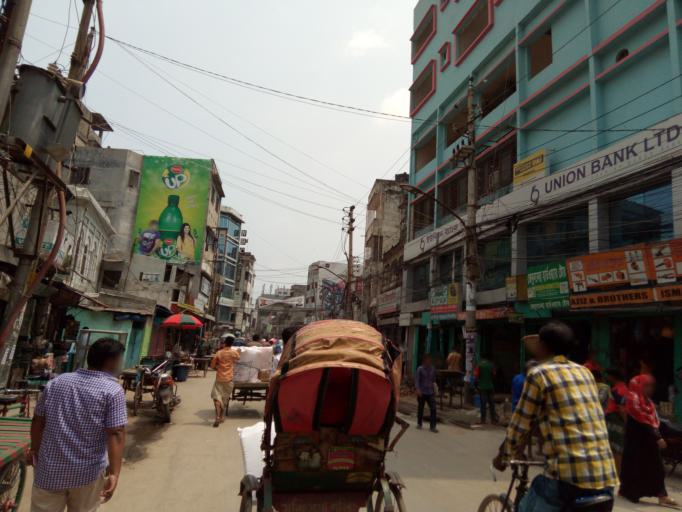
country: BD
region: Dhaka
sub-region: Dhaka
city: Dhaka
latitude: 23.7160
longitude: 90.4115
